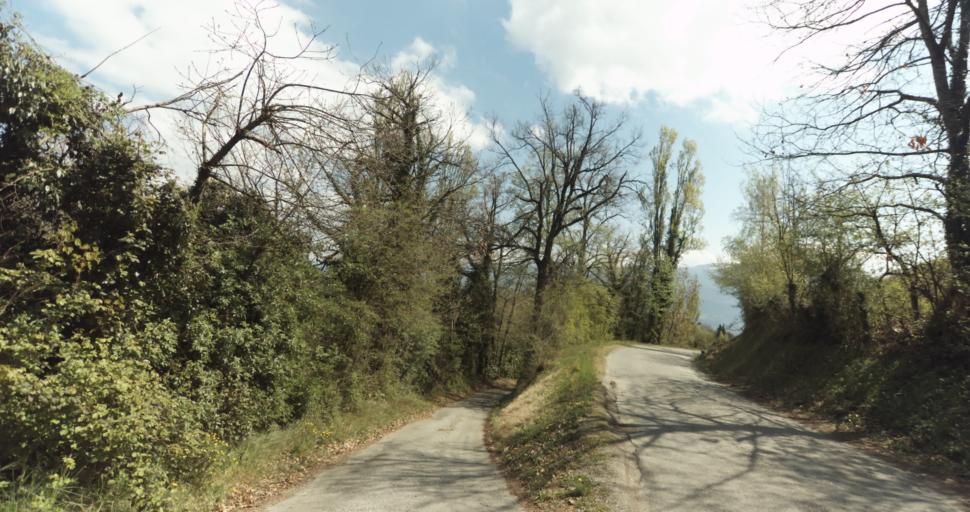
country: FR
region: Rhone-Alpes
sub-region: Departement de l'Isere
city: Saint-Marcellin
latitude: 45.1638
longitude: 5.3124
